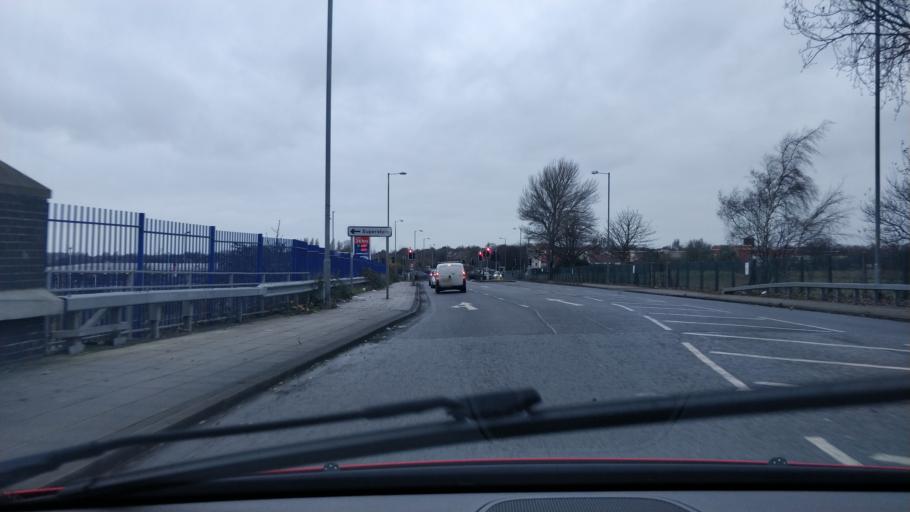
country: GB
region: England
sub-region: Sefton
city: Litherland
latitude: 53.4674
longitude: -2.9943
